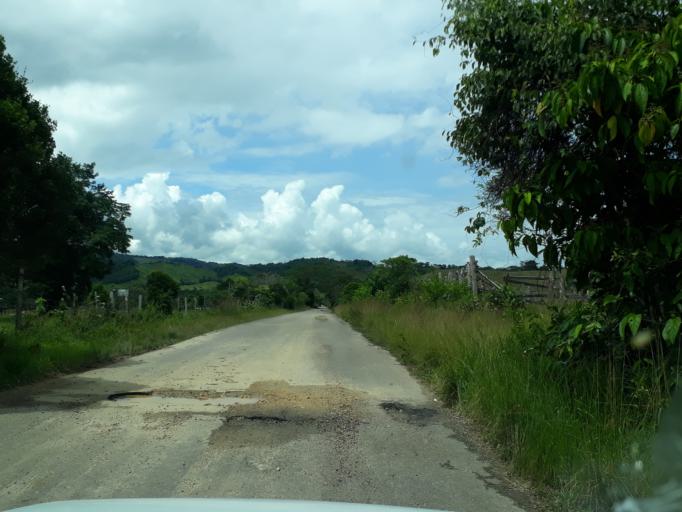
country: CO
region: Cundinamarca
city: Medina
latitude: 4.6031
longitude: -73.2987
